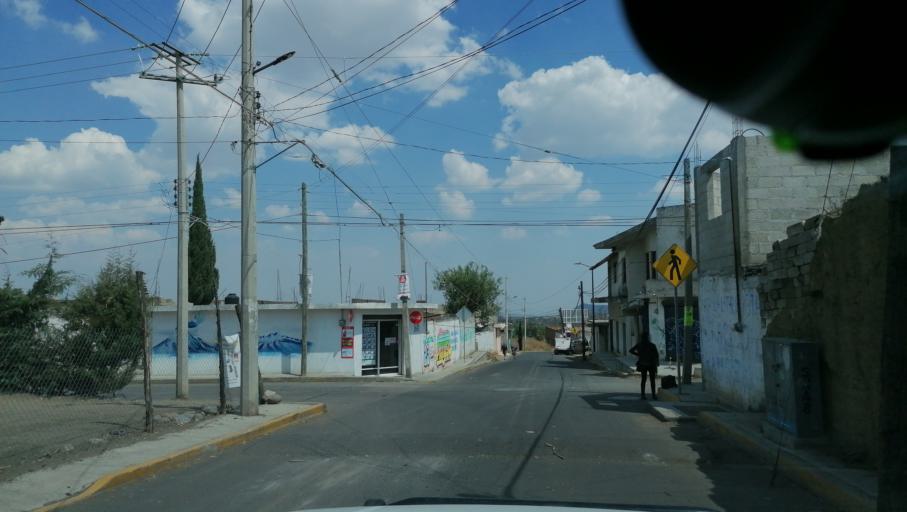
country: MX
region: Puebla
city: San Andres Calpan
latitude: 19.1028
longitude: -98.4737
